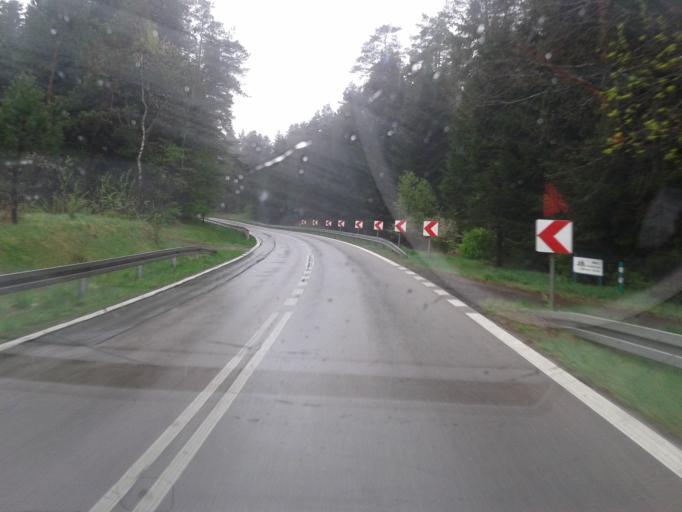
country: PL
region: Lublin Voivodeship
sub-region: Powiat tomaszowski
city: Belzec
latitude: 50.3756
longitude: 23.3811
